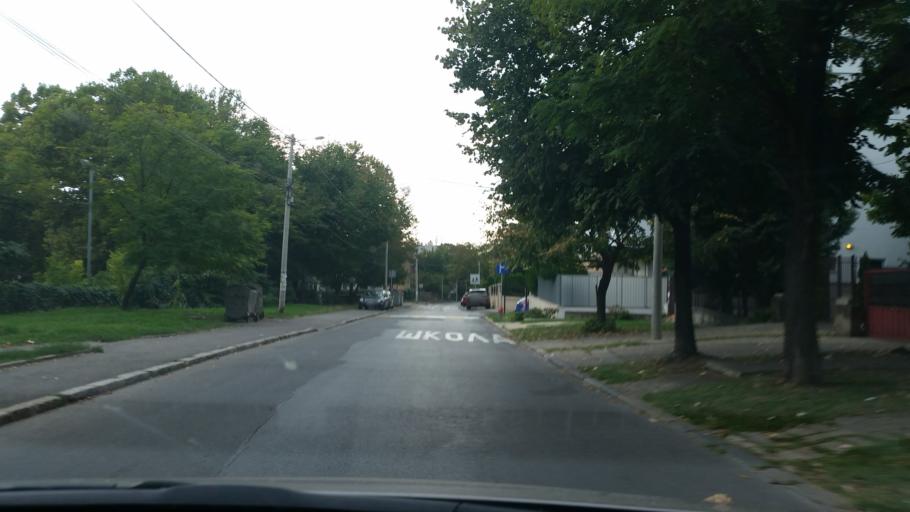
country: RS
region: Central Serbia
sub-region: Belgrade
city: Palilula
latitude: 44.8056
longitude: 20.4986
